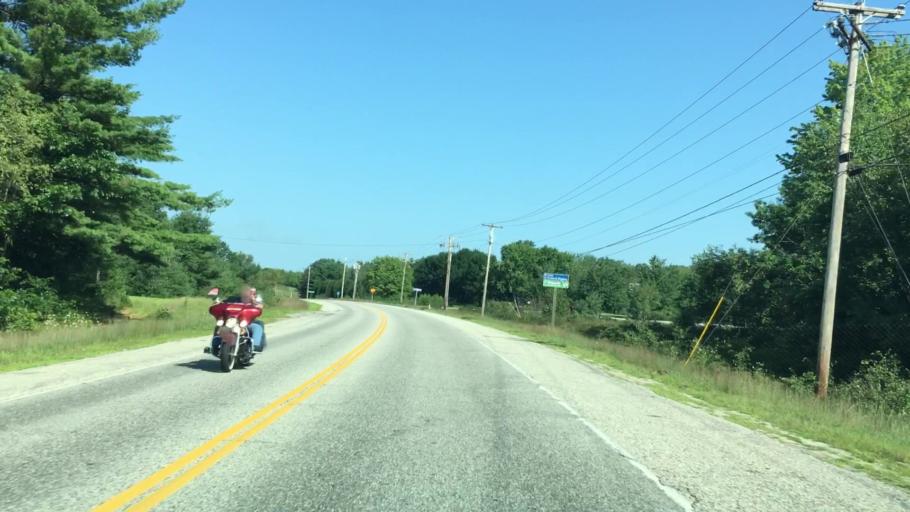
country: US
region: Maine
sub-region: Androscoggin County
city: Minot
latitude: 44.0384
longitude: -70.2757
